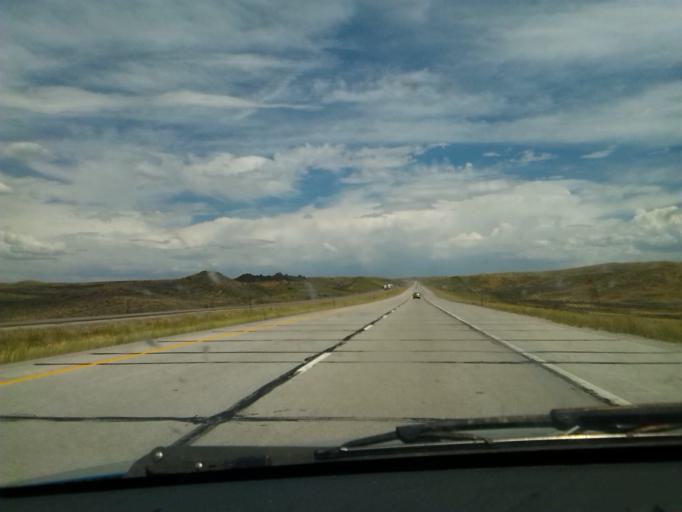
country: US
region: Wyoming
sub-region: Carbon County
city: Saratoga
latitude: 41.7304
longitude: -106.6956
